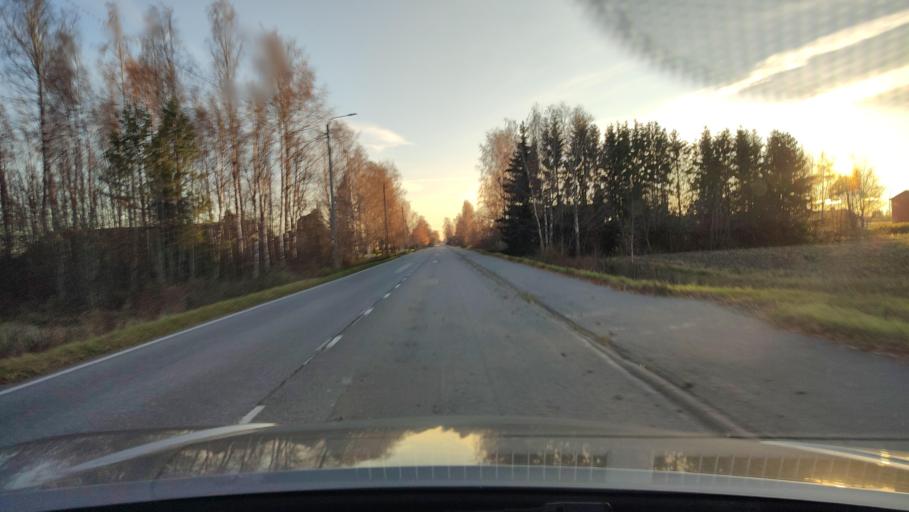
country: FI
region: Ostrobothnia
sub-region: Sydosterbotten
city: Naerpes
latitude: 62.5495
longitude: 21.4013
